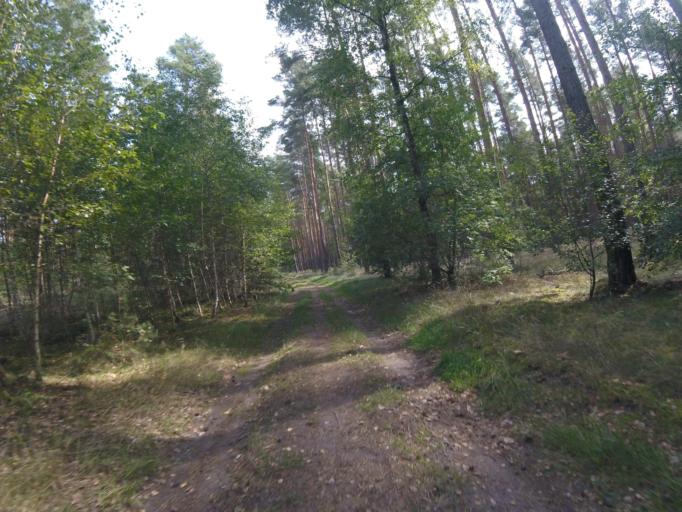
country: DE
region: Brandenburg
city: Bestensee
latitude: 52.2681
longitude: 13.6629
